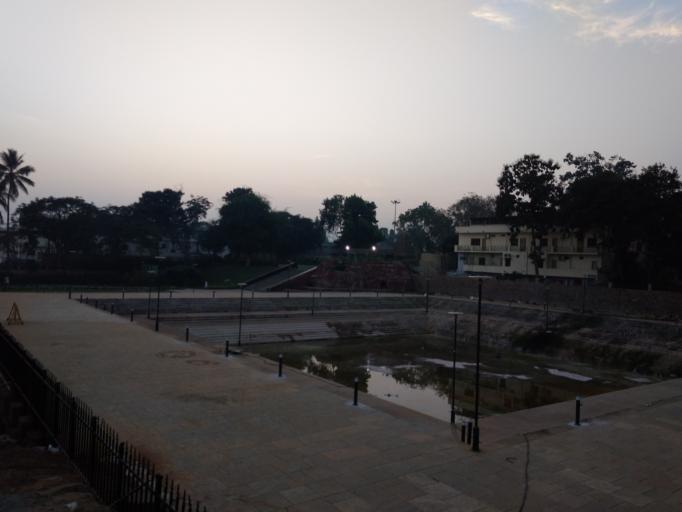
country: IN
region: Andhra Pradesh
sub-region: Kurnool
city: Srisailam
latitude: 16.0750
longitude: 78.8690
